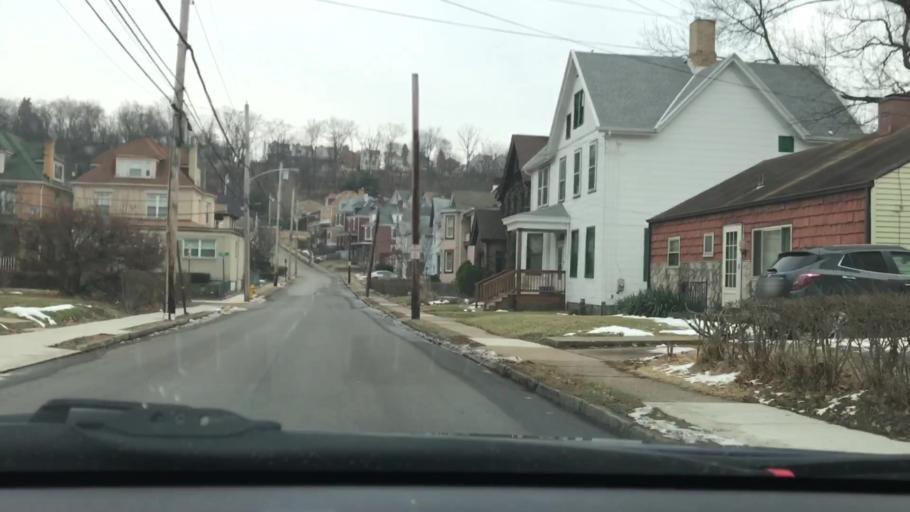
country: US
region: Pennsylvania
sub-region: Allegheny County
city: Ingram
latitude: 40.4469
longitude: -80.0668
